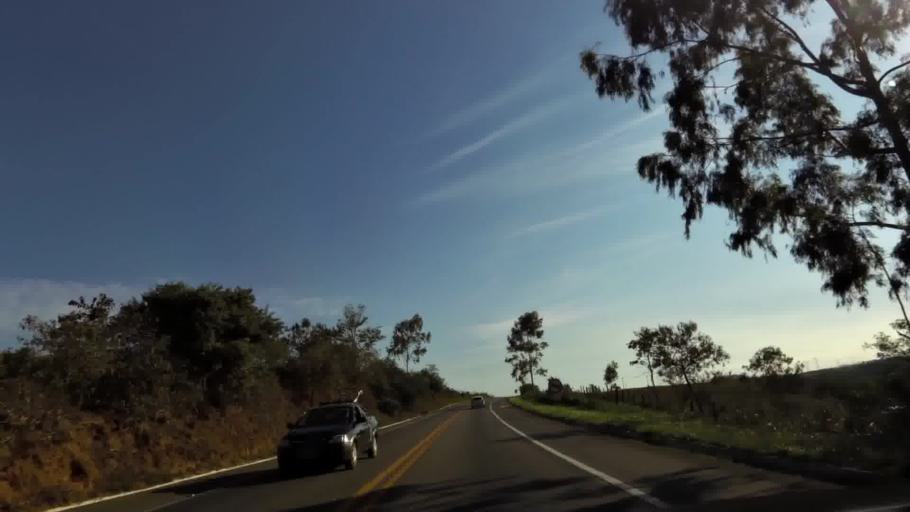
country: BR
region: Espirito Santo
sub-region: Viana
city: Viana
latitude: -20.4873
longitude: -40.4767
